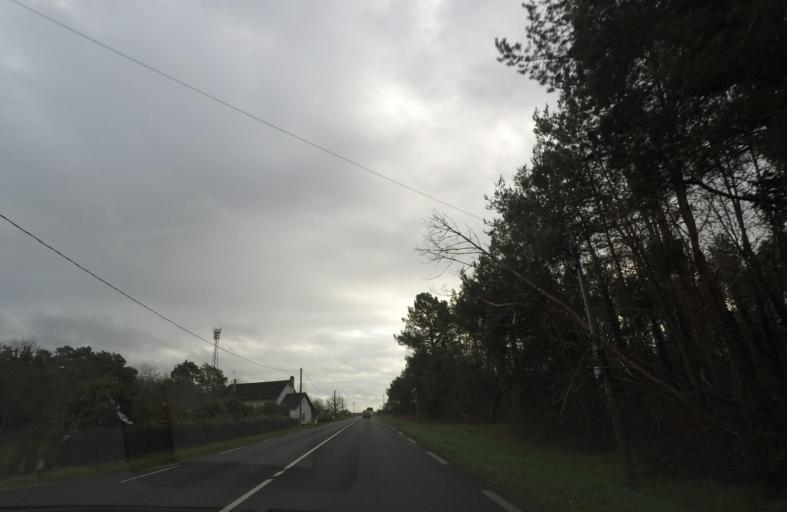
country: FR
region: Centre
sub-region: Departement du Loir-et-Cher
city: Mur-de-Sologne
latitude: 47.4179
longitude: 1.5944
